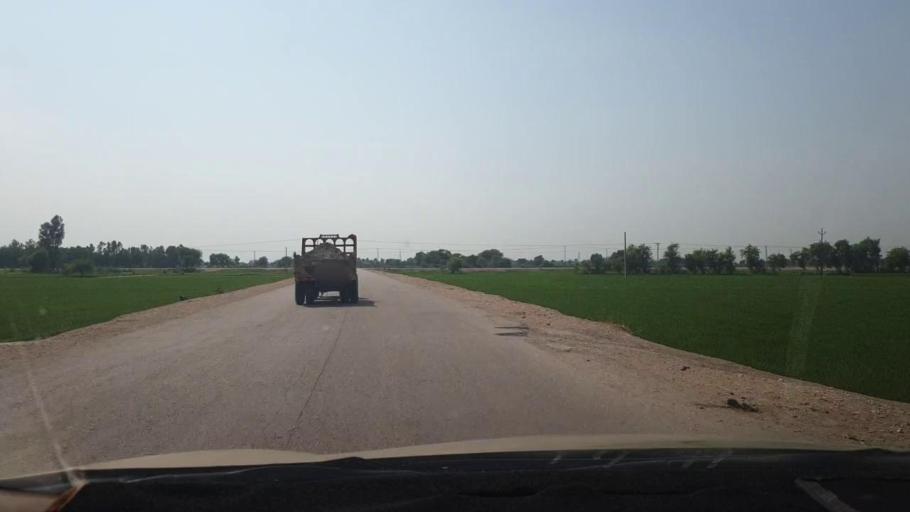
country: PK
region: Sindh
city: Larkana
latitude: 27.6110
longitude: 68.2359
